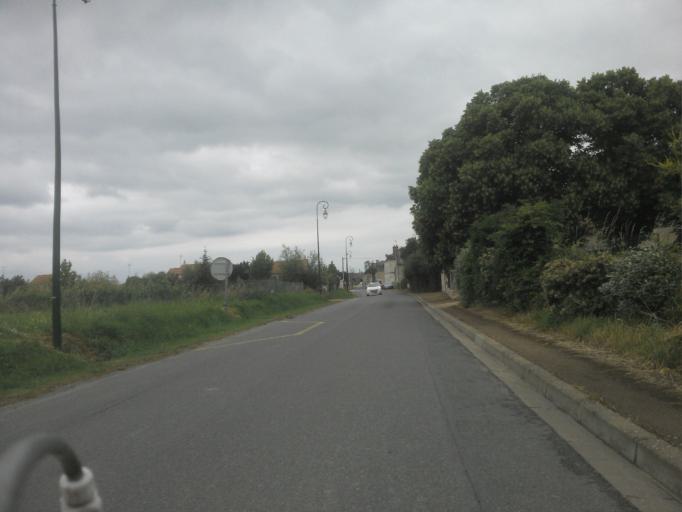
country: FR
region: Pays de la Loire
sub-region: Departement de Maine-et-Loire
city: Breze
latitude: 47.1070
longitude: -0.0235
